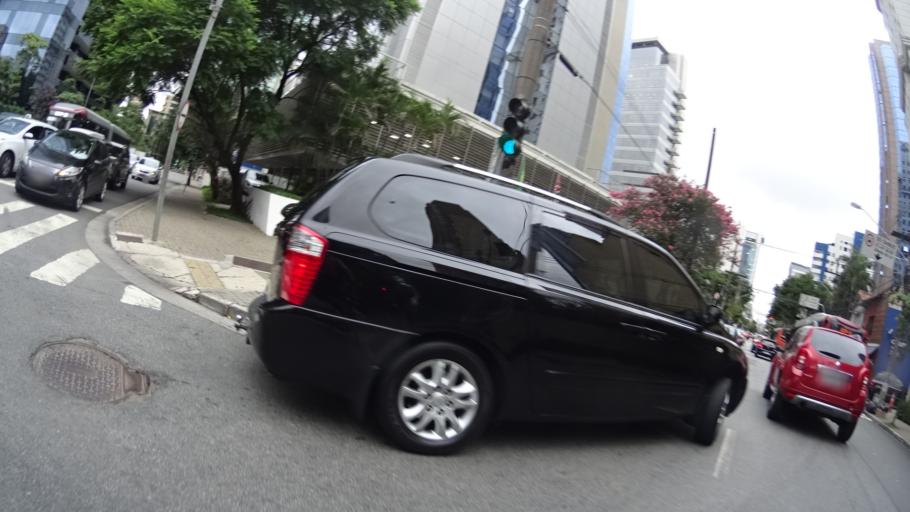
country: BR
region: Sao Paulo
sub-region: Sao Paulo
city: Sao Paulo
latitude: -23.5856
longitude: -46.6815
